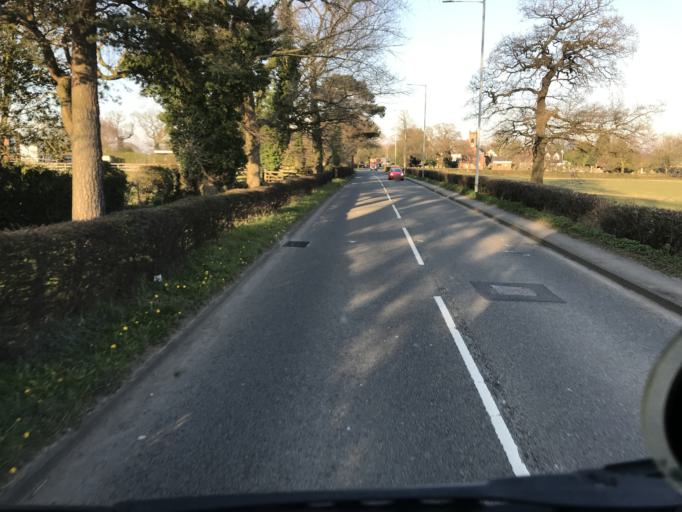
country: GB
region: England
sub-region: Borough of Stockport
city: Bramhall
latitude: 53.3371
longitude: -2.1765
